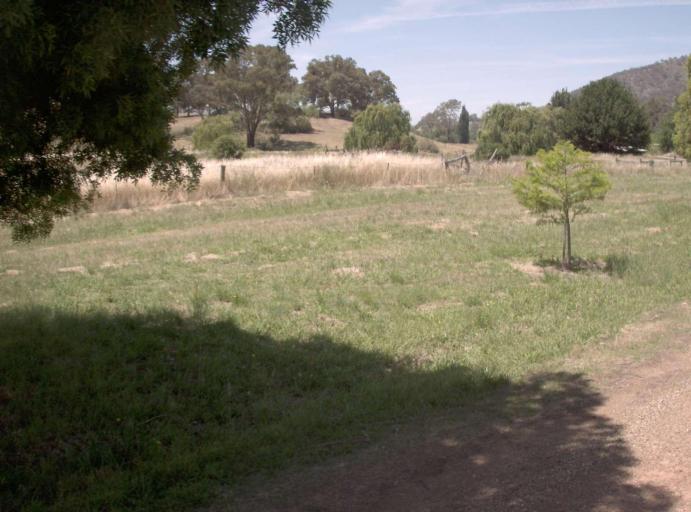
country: AU
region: Victoria
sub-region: East Gippsland
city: Bairnsdale
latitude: -37.2529
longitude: 147.7117
